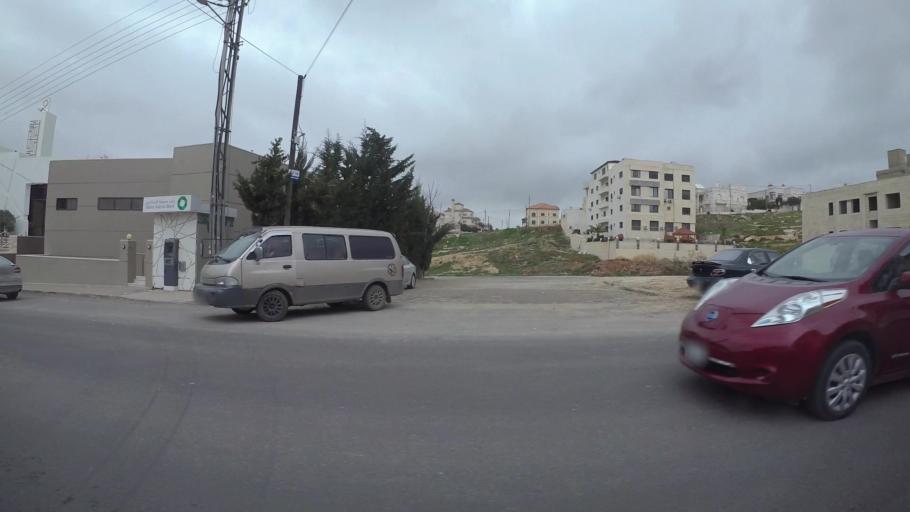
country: JO
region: Amman
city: Wadi as Sir
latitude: 31.9901
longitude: 35.8373
